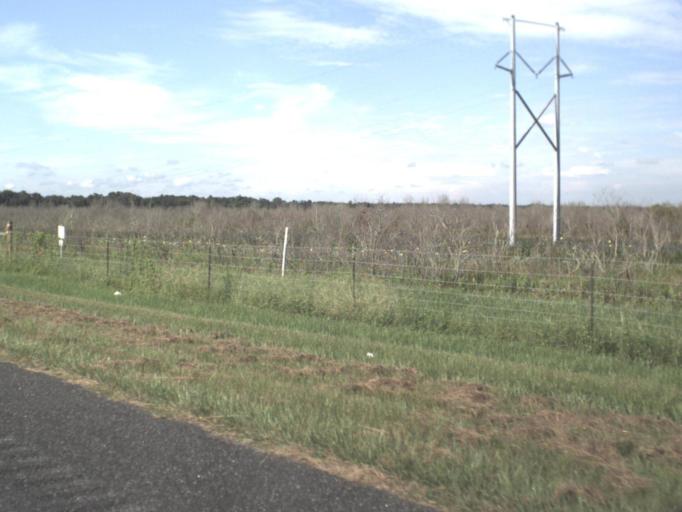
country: US
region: Florida
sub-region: Alachua County
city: Gainesville
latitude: 29.5700
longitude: -82.3343
